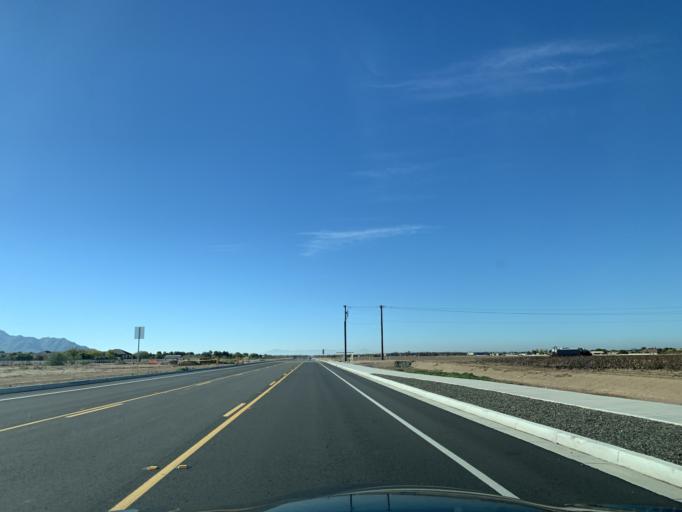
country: US
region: Arizona
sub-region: Maricopa County
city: Queen Creek
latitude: 33.2195
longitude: -111.6160
